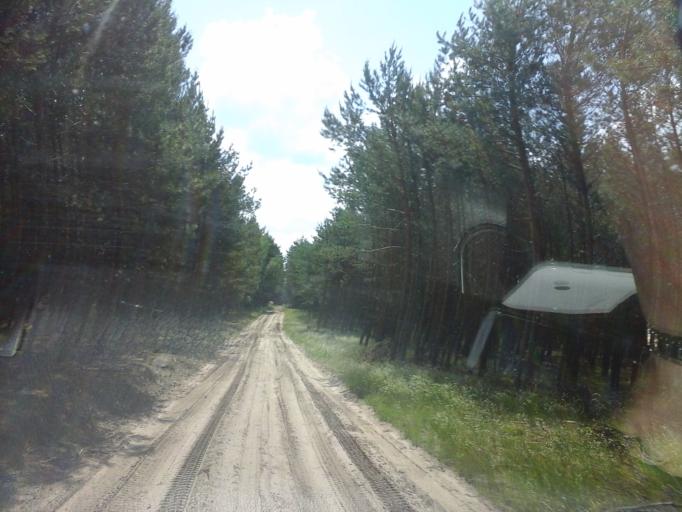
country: PL
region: West Pomeranian Voivodeship
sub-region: Powiat choszczenski
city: Bierzwnik
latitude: 53.1194
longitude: 15.6817
